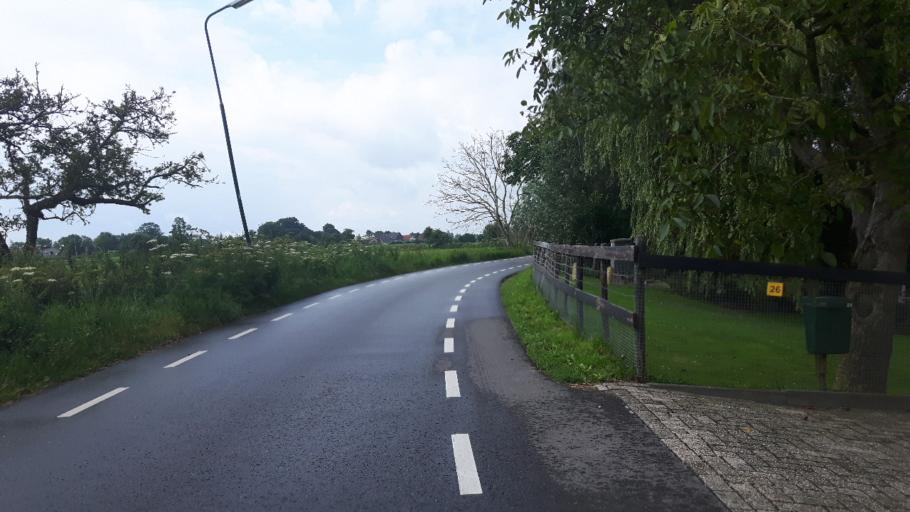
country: NL
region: Utrecht
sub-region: Gemeente Montfoort
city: Montfoort
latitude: 52.0285
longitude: 4.9226
